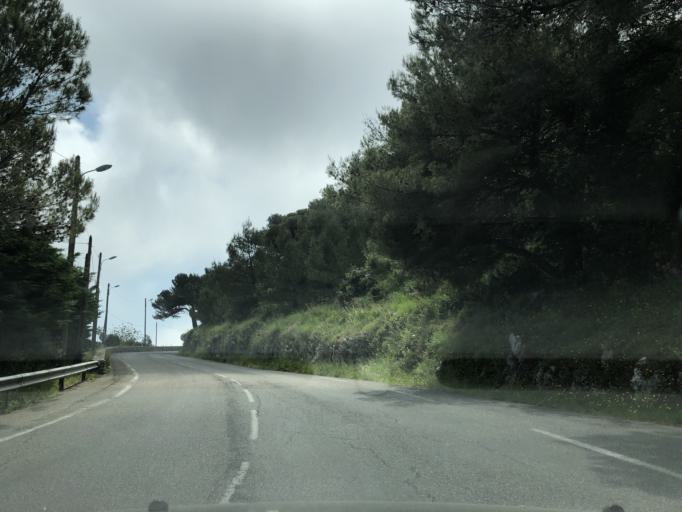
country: FR
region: Provence-Alpes-Cote d'Azur
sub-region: Departement des Alpes-Maritimes
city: Beaulieu-sur-Mer
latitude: 43.7308
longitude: 7.3416
